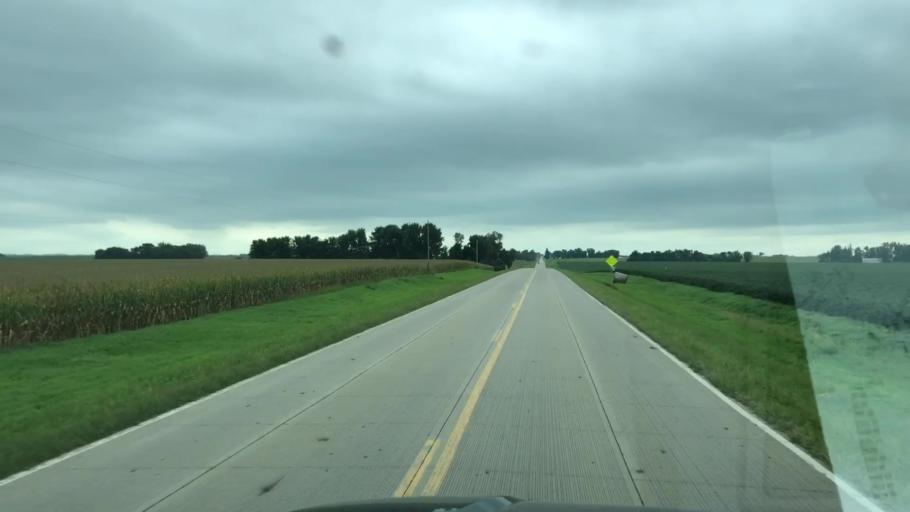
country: US
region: Iowa
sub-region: O'Brien County
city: Sheldon
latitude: 43.1233
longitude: -95.9789
